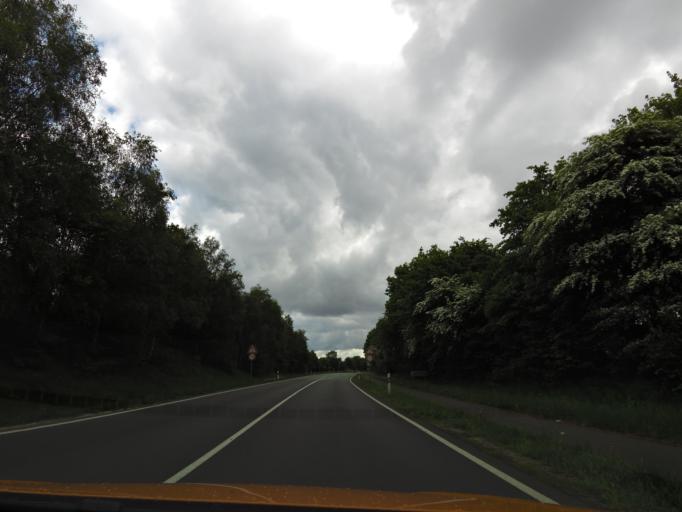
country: DE
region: Lower Saxony
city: Bassum
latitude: 52.8366
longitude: 8.7085
